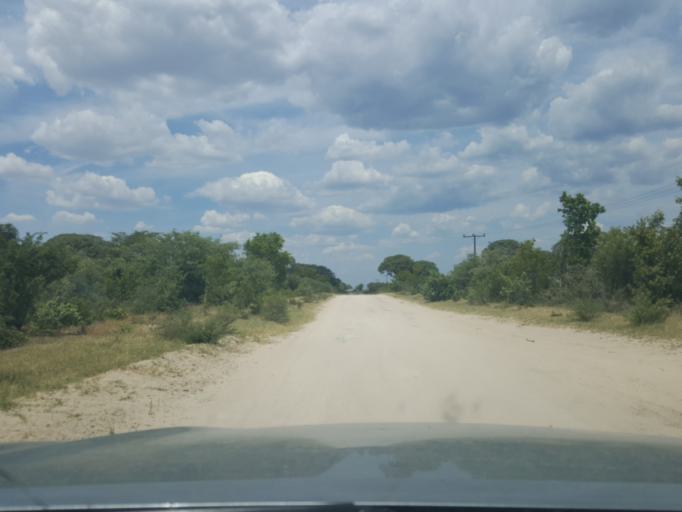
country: BW
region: North West
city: Shakawe
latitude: -18.4798
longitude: 22.1133
